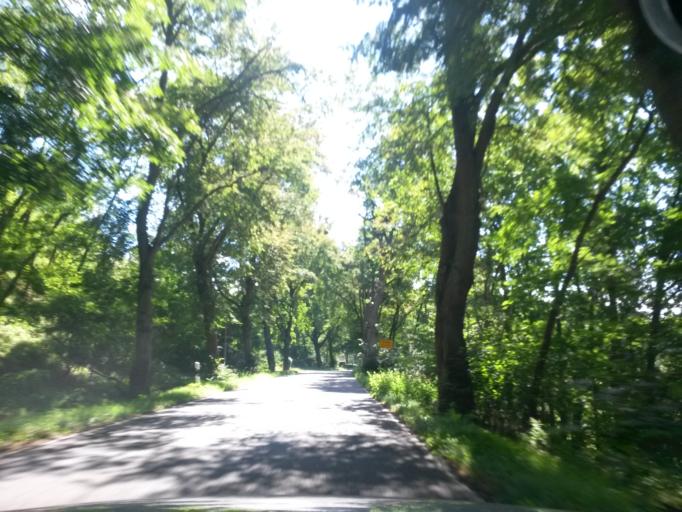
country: DE
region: Brandenburg
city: Schoneberg
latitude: 52.9823
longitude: 14.1104
